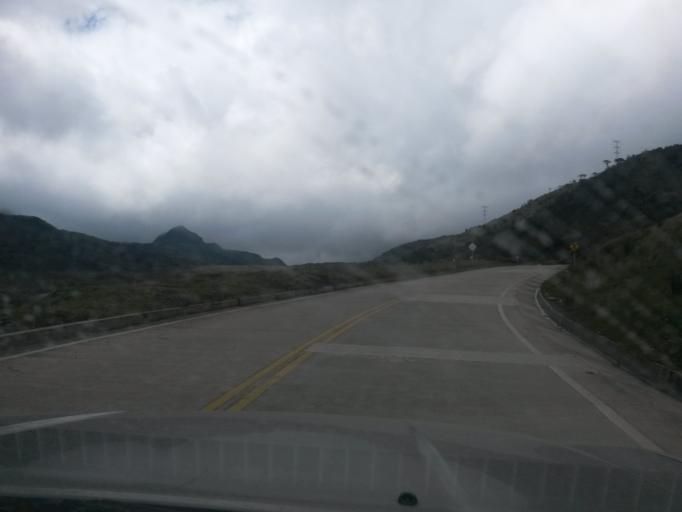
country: CO
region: Cauca
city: Totoro
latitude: 2.4965
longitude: -76.2362
